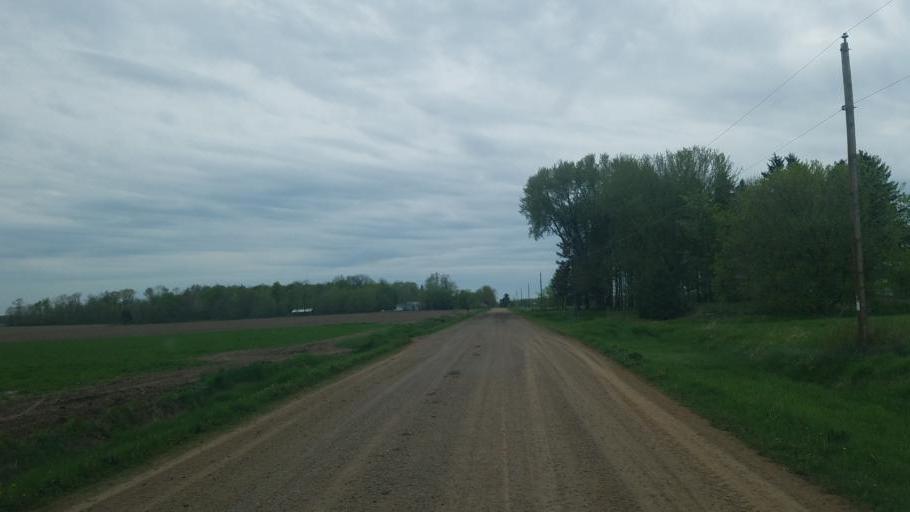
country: US
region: Wisconsin
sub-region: Clark County
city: Loyal
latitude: 44.6312
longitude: -90.4174
